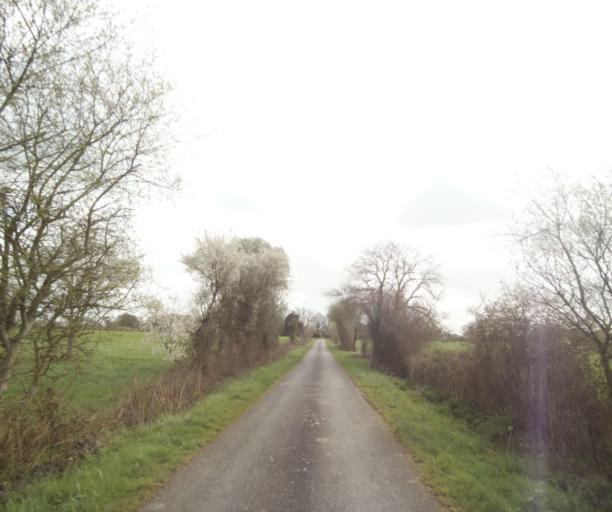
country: FR
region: Pays de la Loire
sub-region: Departement de la Loire-Atlantique
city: Bouvron
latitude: 47.4126
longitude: -1.8830
